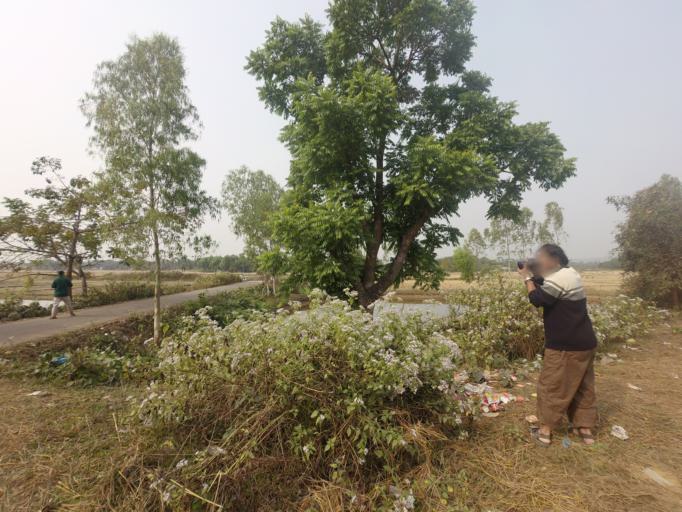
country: BD
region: Dhaka
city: Netrakona
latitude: 25.1576
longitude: 90.6585
